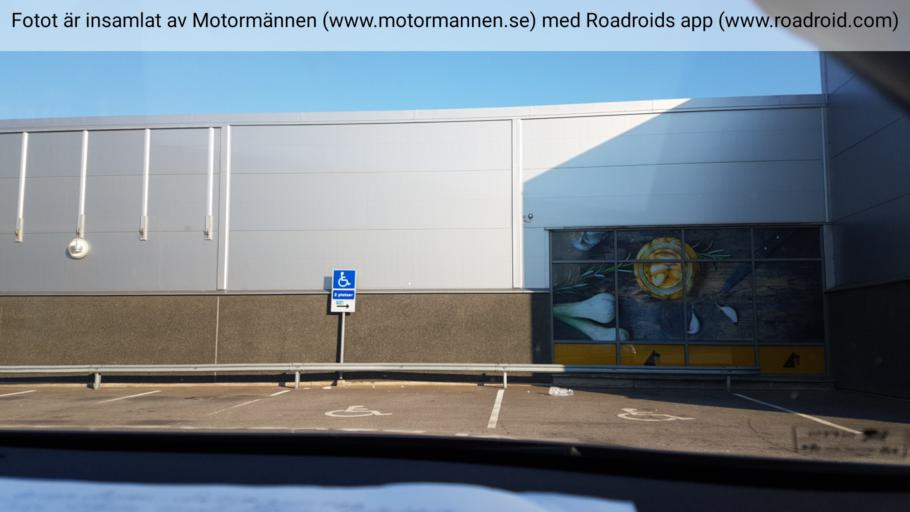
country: SE
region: Vaestra Goetaland
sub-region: Skovde Kommun
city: Skoevde
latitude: 58.3866
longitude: 13.8619
